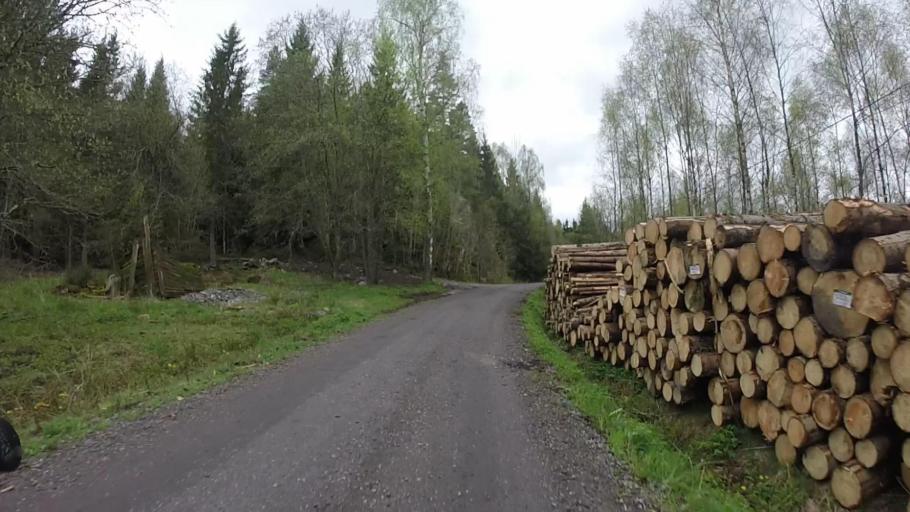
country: SE
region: Vaestra Goetaland
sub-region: Trollhattan
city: Sjuntorp
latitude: 58.2139
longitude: 12.2134
